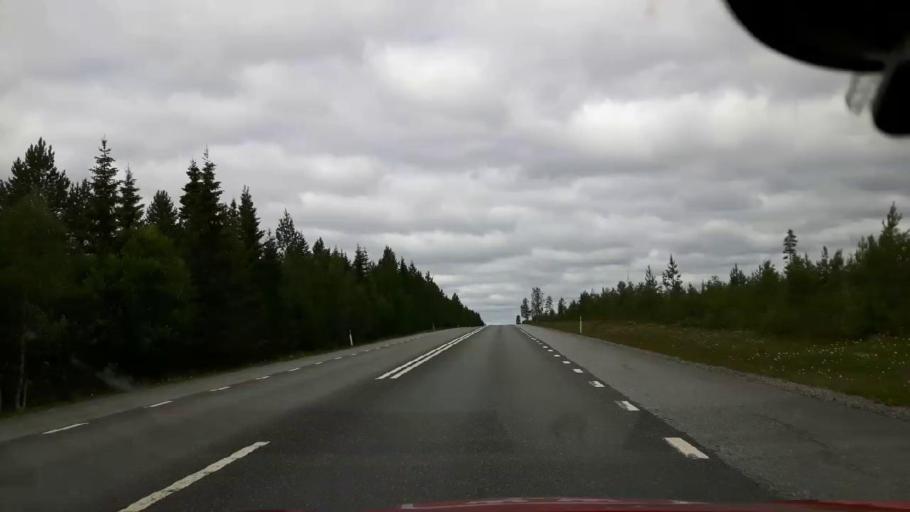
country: SE
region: Vaesternorrland
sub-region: Ange Kommun
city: Ange
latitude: 62.6778
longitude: 15.5945
